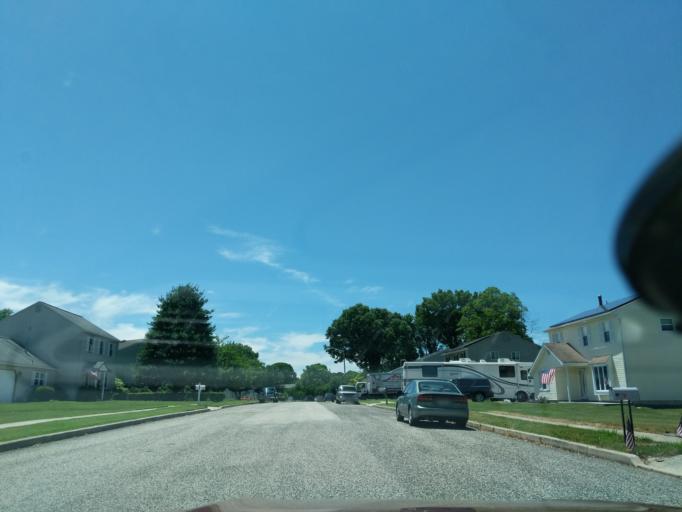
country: US
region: New Jersey
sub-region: Gloucester County
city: Woodbury Heights
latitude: 39.8171
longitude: -75.1155
